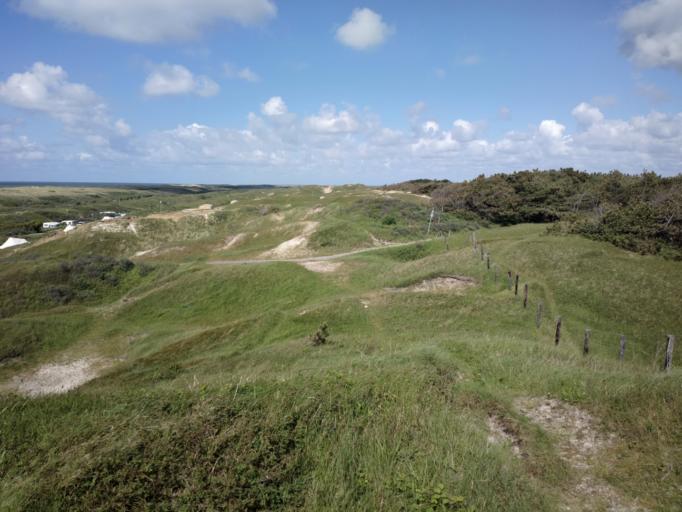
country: NL
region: North Holland
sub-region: Gemeente Texel
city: Den Burg
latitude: 53.1055
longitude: 4.7645
